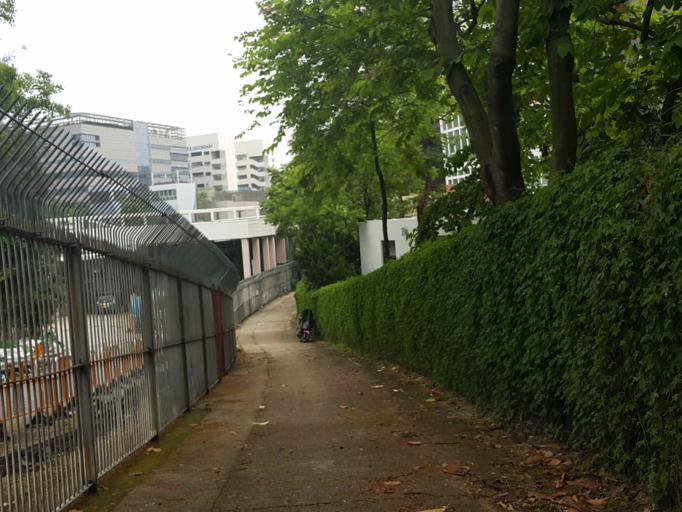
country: HK
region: Wong Tai Sin
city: Wong Tai Sin
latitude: 22.3382
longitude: 114.1747
